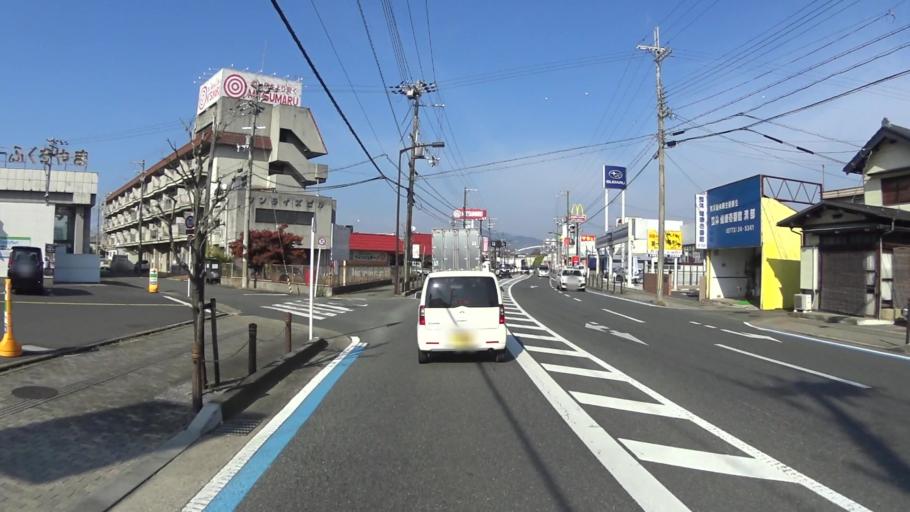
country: JP
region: Kyoto
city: Fukuchiyama
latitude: 35.2933
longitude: 135.1347
